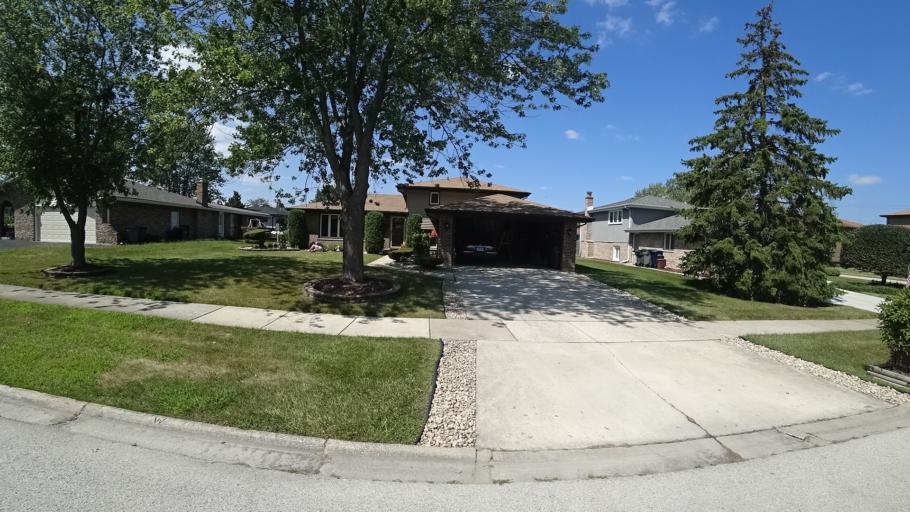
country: US
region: Illinois
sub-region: Cook County
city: Orland Park
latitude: 41.6361
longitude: -87.8362
